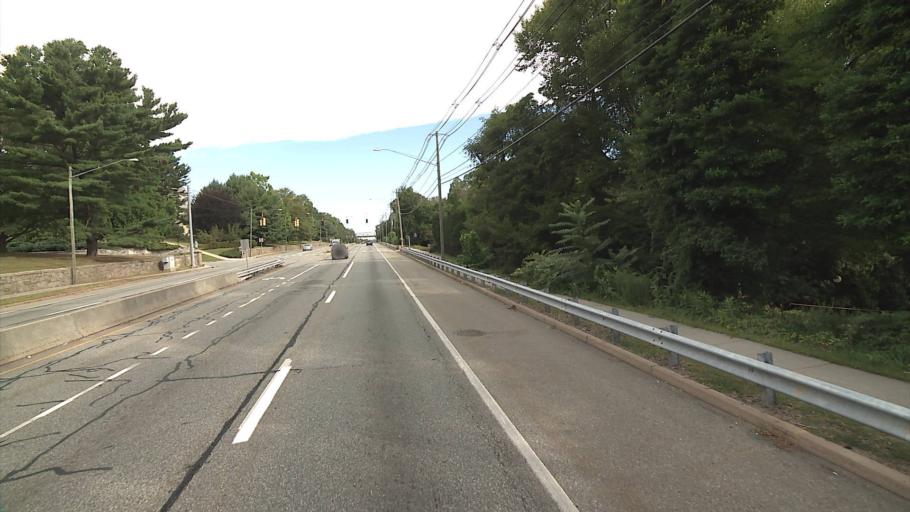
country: US
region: Connecticut
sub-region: New London County
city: New London
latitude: 41.3778
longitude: -72.1033
